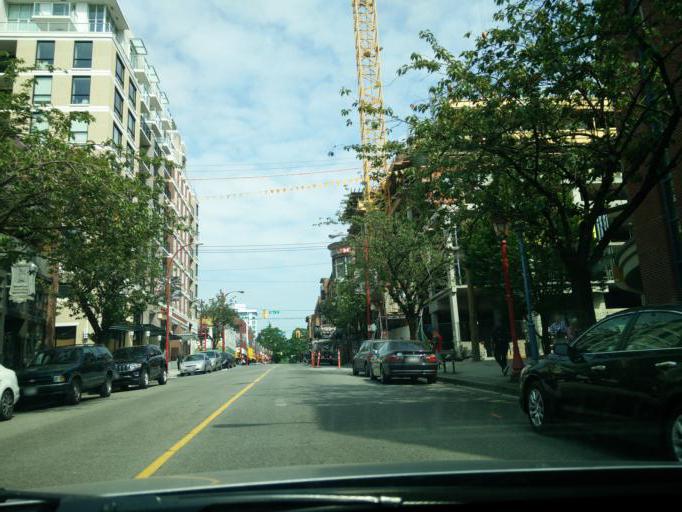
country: CA
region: British Columbia
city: West End
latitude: 49.2795
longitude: -123.1010
